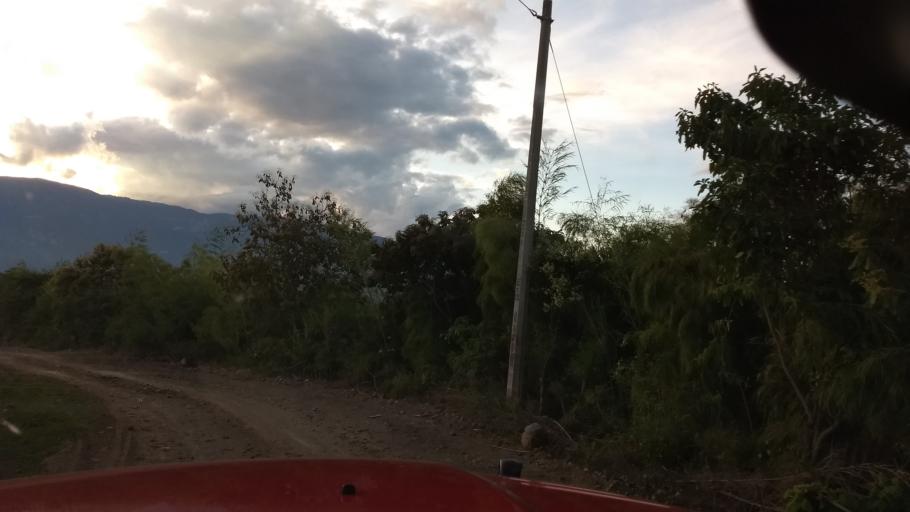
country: MX
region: Colima
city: Suchitlan
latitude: 19.4921
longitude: -103.7855
